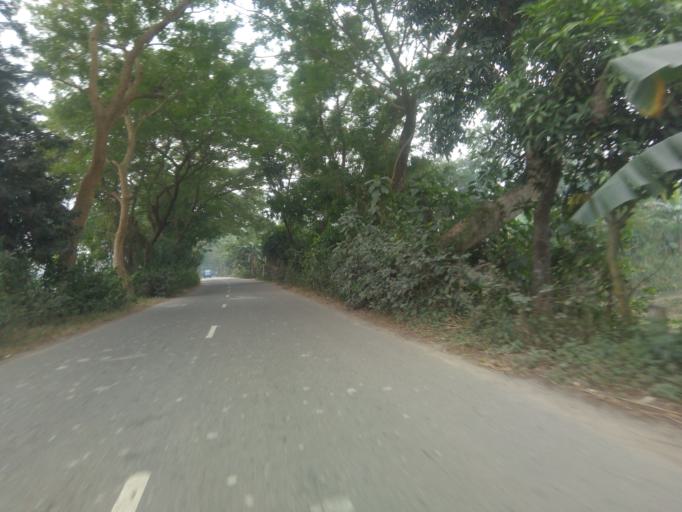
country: BD
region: Dhaka
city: Narayanganj
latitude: 23.5222
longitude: 90.4711
